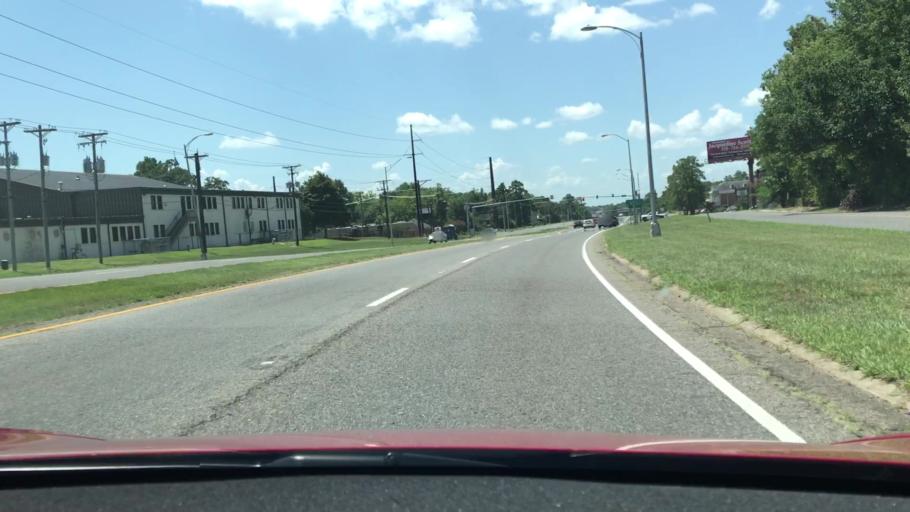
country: US
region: Louisiana
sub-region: Bossier Parish
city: Bossier City
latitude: 32.5016
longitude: -93.7250
